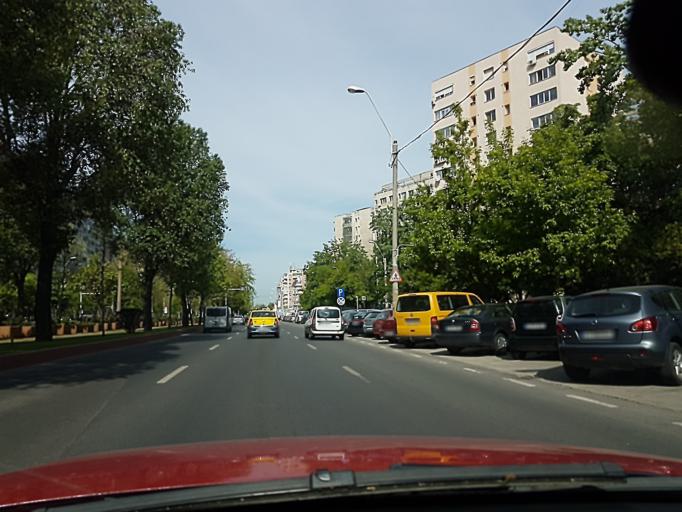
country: RO
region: Bucuresti
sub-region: Municipiul Bucuresti
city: Bucharest
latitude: 44.4187
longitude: 26.1433
